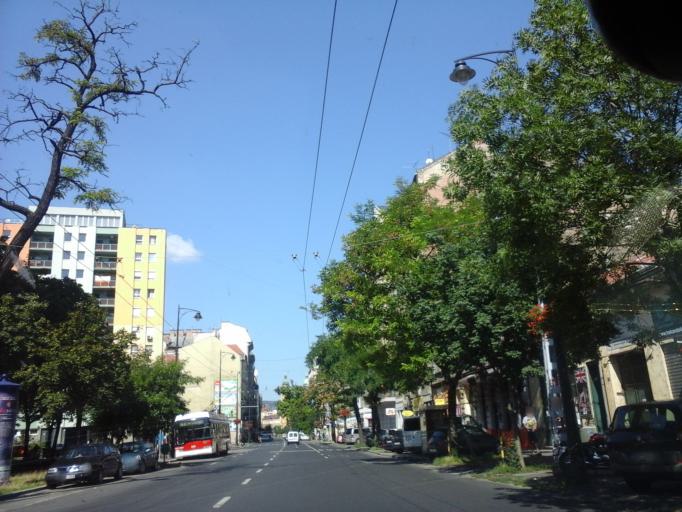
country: HU
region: Budapest
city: Budapest VIII. keruelet
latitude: 47.4890
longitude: 19.0818
